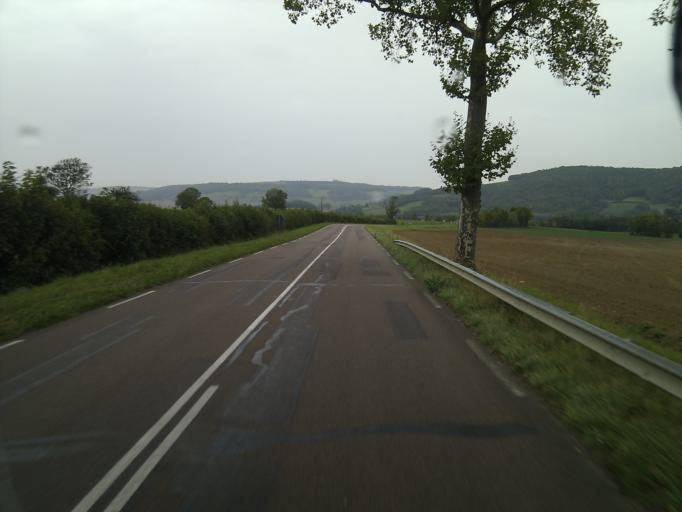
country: FR
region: Bourgogne
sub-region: Departement de la Cote-d'Or
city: Semur-en-Auxois
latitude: 47.4978
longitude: 4.3245
